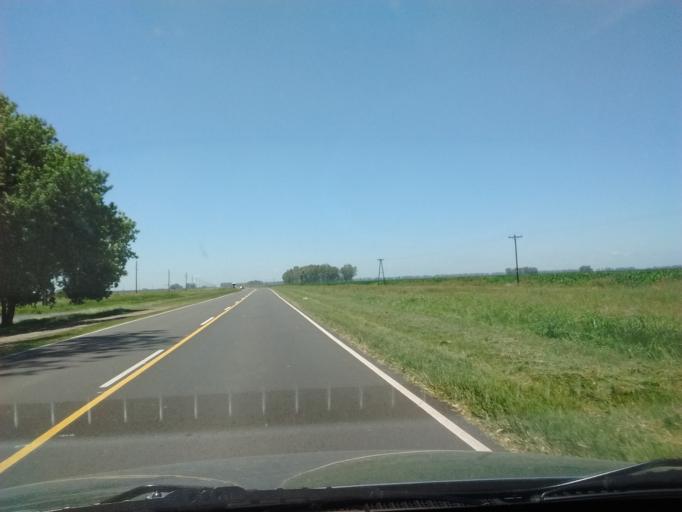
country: AR
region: Entre Rios
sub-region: Departamento de Gualeguay
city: Gualeguay
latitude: -32.9753
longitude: -59.5587
